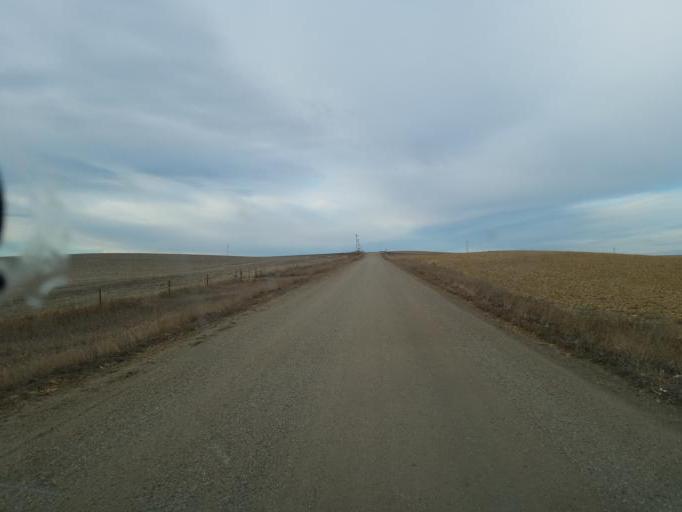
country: US
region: Nebraska
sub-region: Knox County
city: Bloomfield
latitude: 42.5833
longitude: -97.6779
